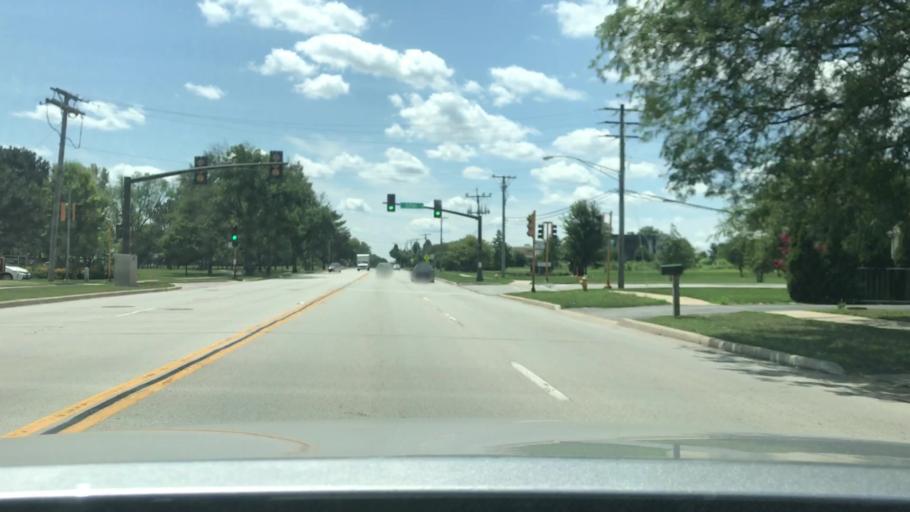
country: US
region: Illinois
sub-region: DuPage County
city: Darien
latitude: 41.7662
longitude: -88.0083
